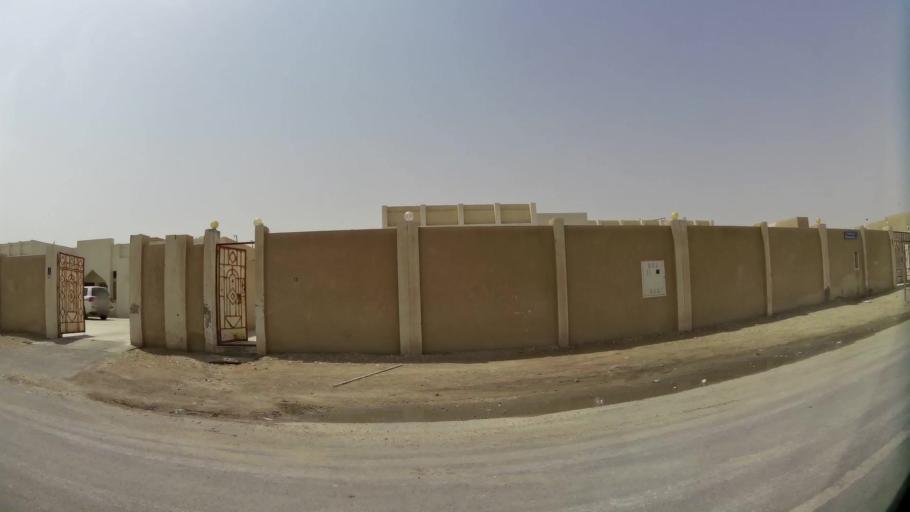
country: QA
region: Baladiyat ar Rayyan
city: Ar Rayyan
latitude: 25.2278
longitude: 51.4116
